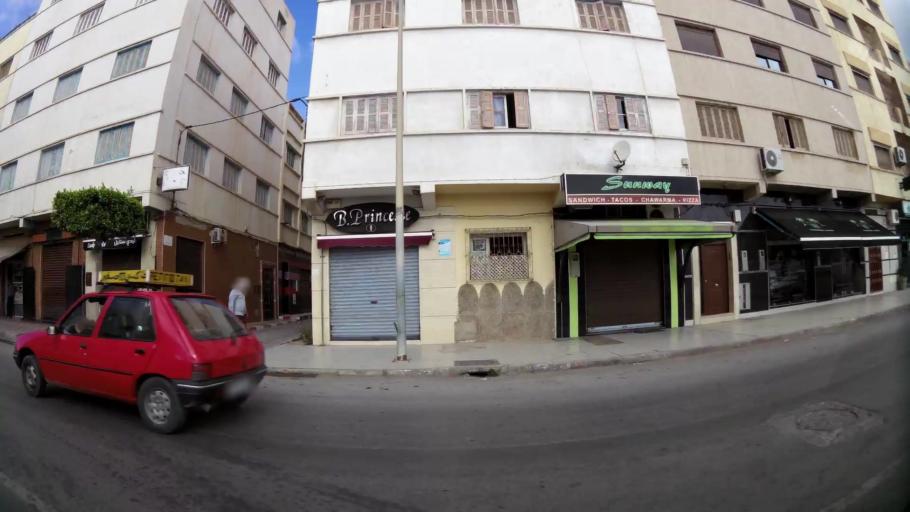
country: MA
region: Oriental
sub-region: Nador
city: Nador
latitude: 35.1704
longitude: -2.9247
